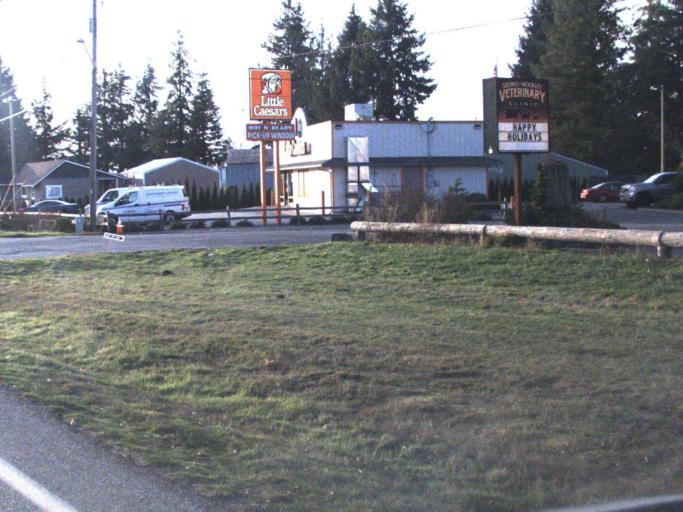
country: US
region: Washington
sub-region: Skagit County
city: Sedro-Woolley
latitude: 48.5121
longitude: -122.2186
